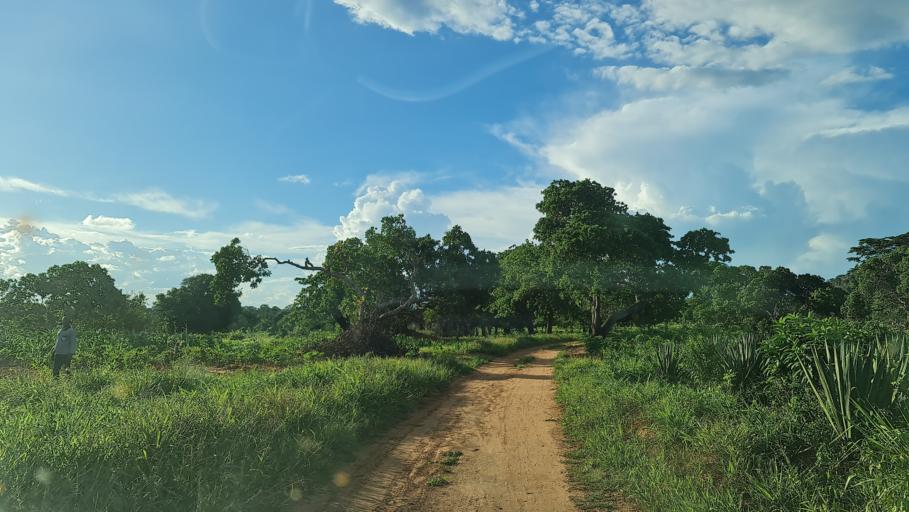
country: MZ
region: Nampula
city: Ilha de Mocambique
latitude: -14.9512
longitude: 40.1702
